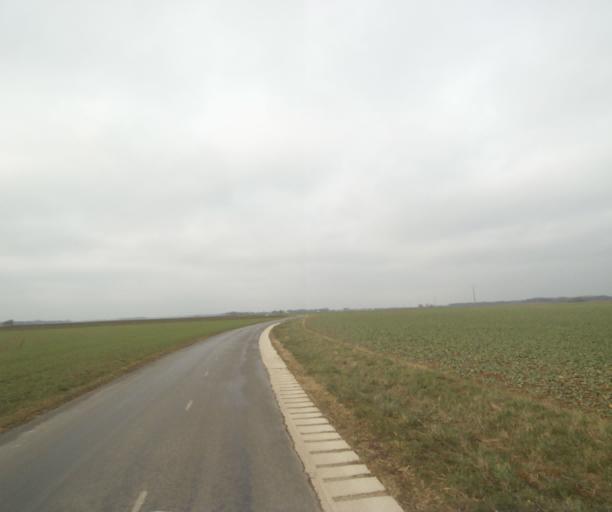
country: FR
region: Champagne-Ardenne
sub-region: Departement de la Haute-Marne
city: Villiers-en-Lieu
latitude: 48.6766
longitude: 4.8624
